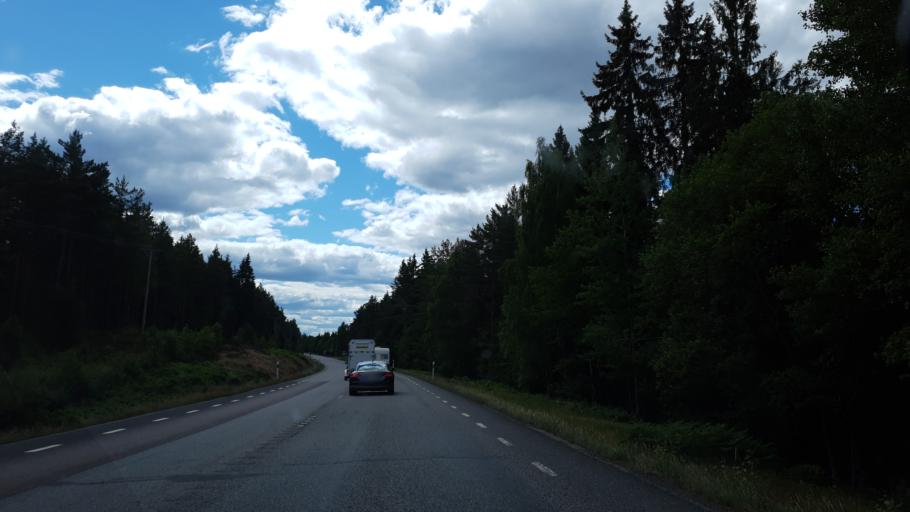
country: SE
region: Kronoberg
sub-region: Vaxjo Kommun
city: Braas
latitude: 57.1525
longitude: 15.1592
